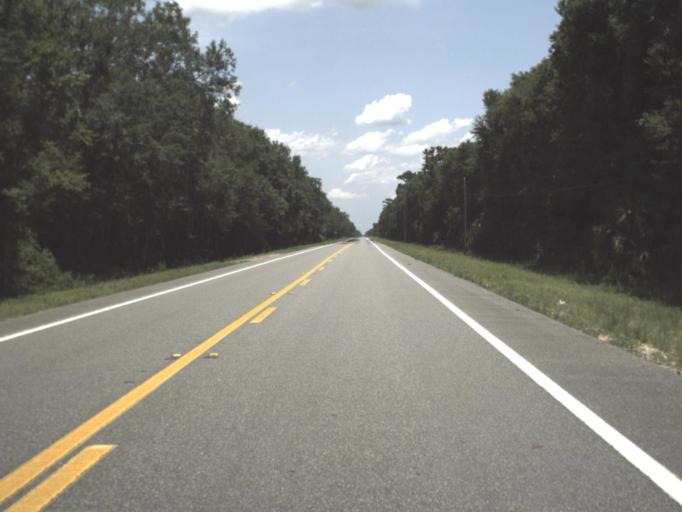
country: US
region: Florida
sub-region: Taylor County
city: Steinhatchee
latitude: 29.7824
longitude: -83.3231
